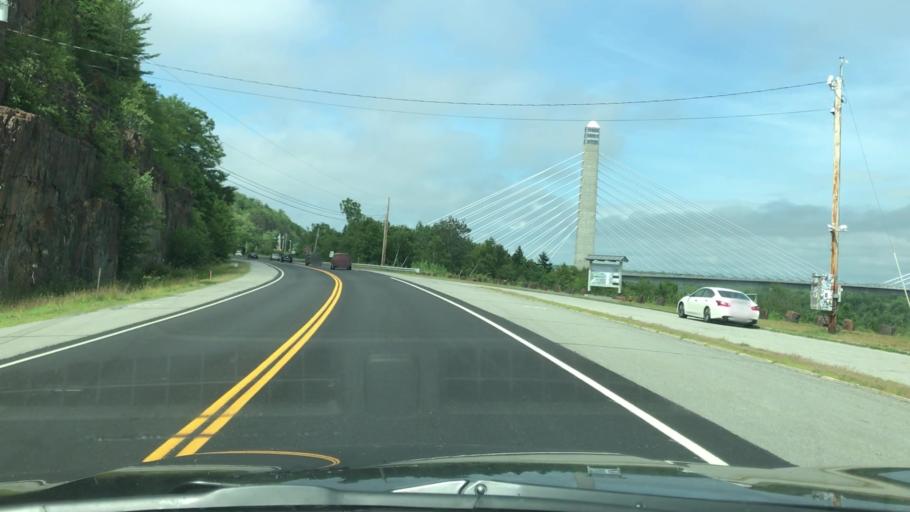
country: US
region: Maine
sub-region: Hancock County
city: Bucksport
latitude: 44.5570
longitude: -68.8080
